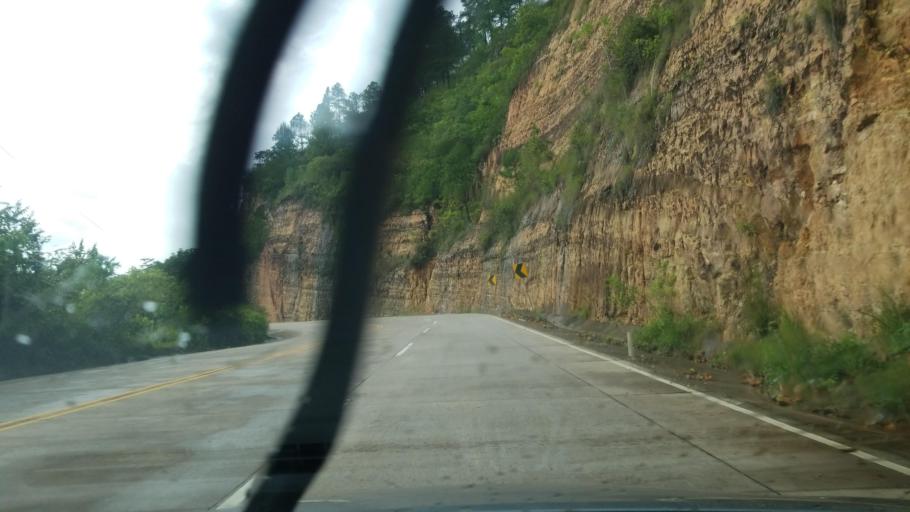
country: HN
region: Copan
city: Copan
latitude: 14.8360
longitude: -89.1856
